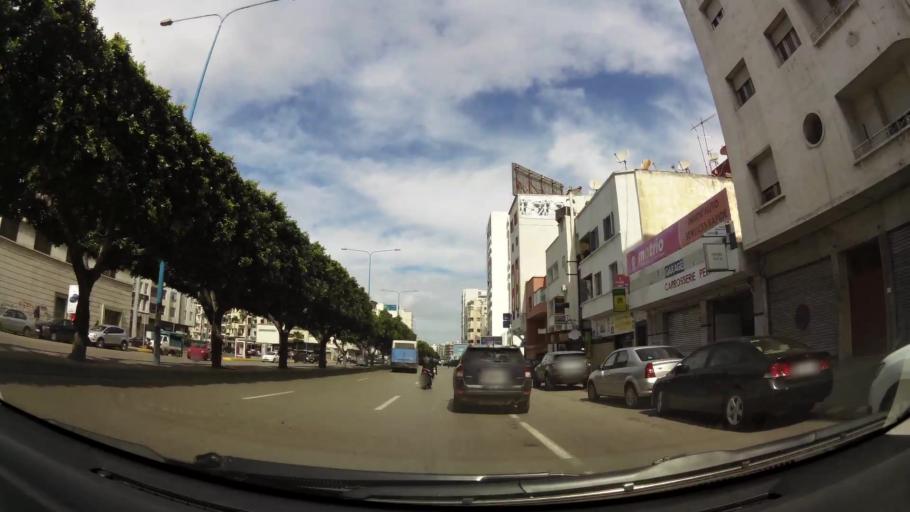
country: MA
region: Grand Casablanca
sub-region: Casablanca
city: Casablanca
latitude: 33.5824
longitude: -7.6400
